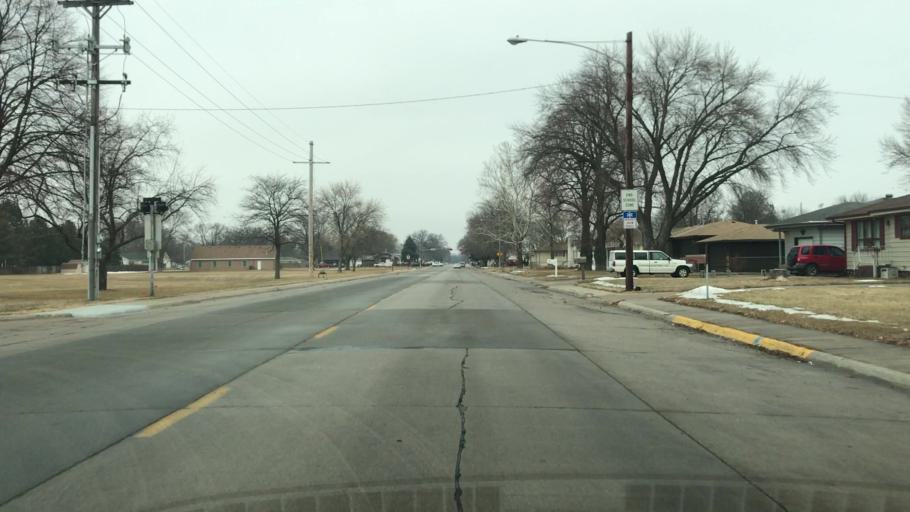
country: US
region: Nebraska
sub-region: Hall County
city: Grand Island
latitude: 40.9357
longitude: -98.3684
